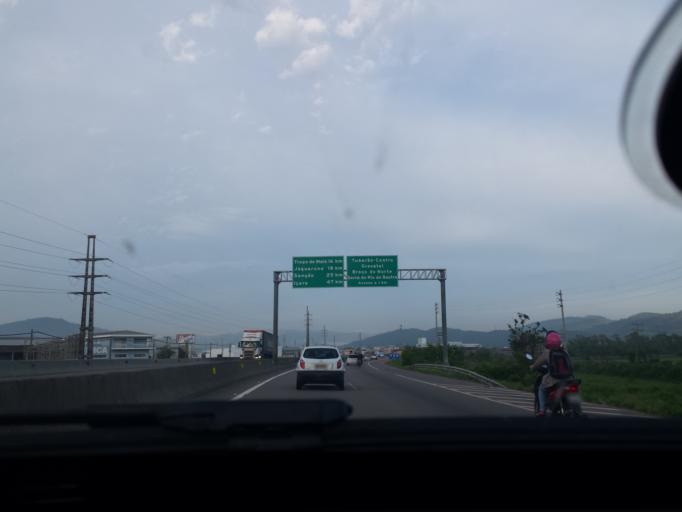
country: BR
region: Santa Catarina
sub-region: Tubarao
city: Tubarao
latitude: -28.4677
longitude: -49.0019
